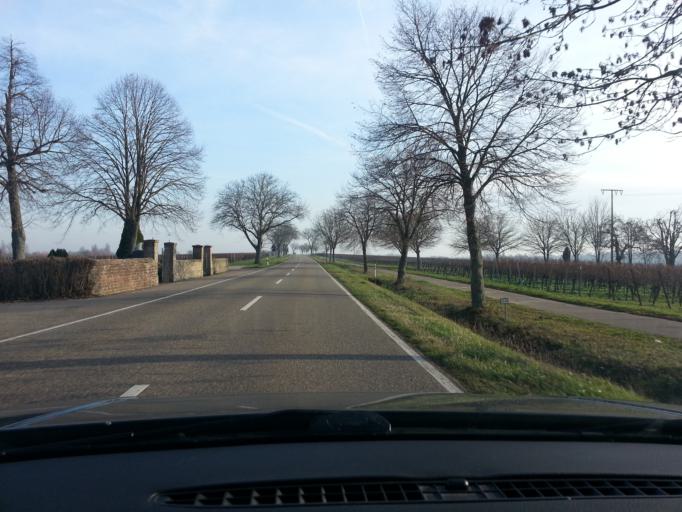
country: DE
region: Rheinland-Pfalz
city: Heuchelheim-Klingen
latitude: 49.1440
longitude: 8.0628
